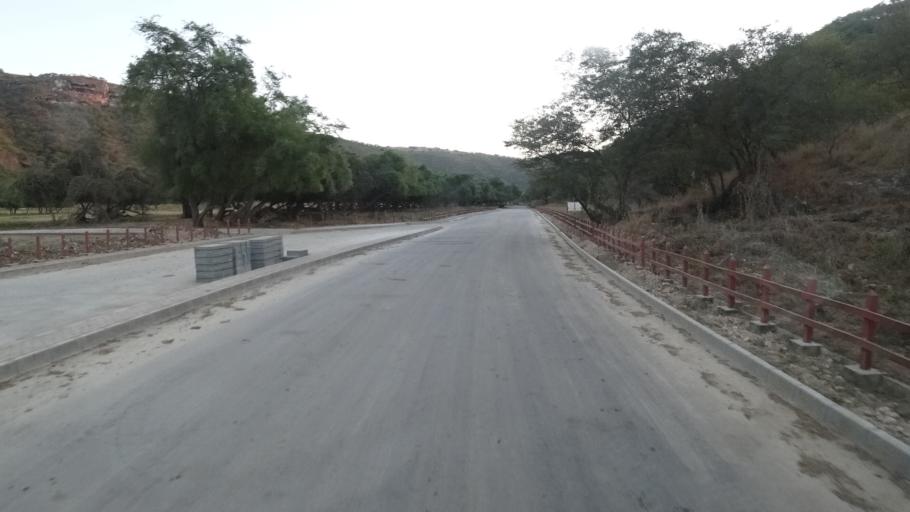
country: OM
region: Zufar
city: Salalah
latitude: 17.0974
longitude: 54.4498
